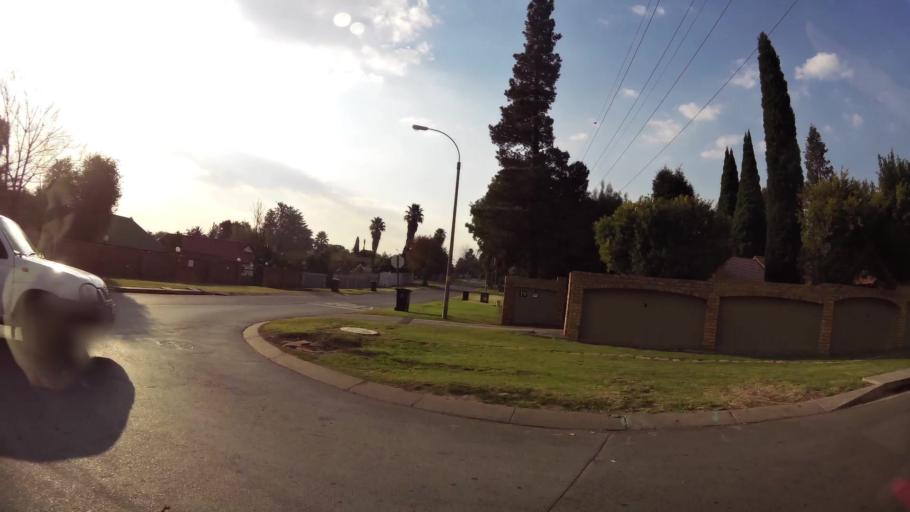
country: ZA
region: Gauteng
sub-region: City of Johannesburg Metropolitan Municipality
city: Modderfontein
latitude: -26.1293
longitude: 28.1921
